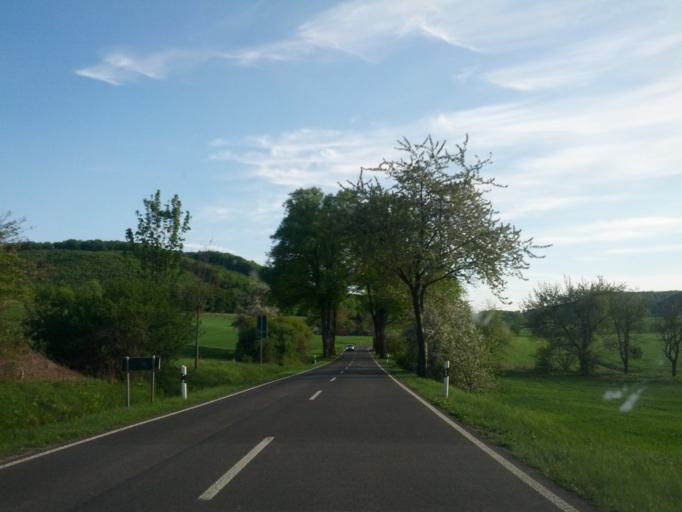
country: DE
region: Thuringia
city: Ifta
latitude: 51.0821
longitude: 10.2157
